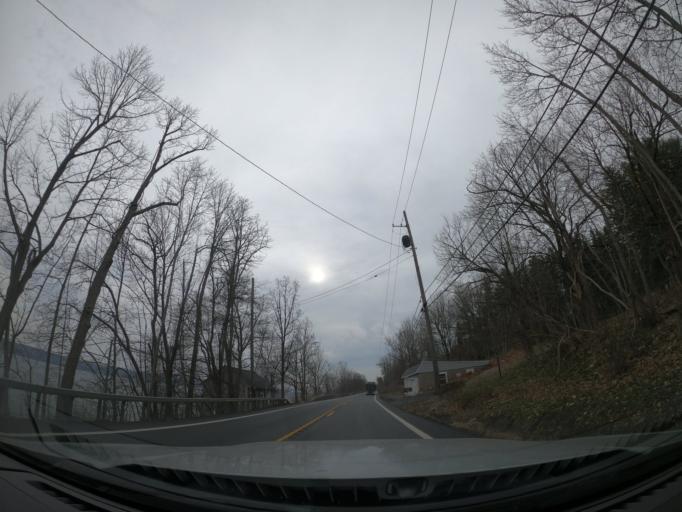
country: US
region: New York
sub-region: Cayuga County
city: Melrose Park
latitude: 42.8539
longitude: -76.5309
